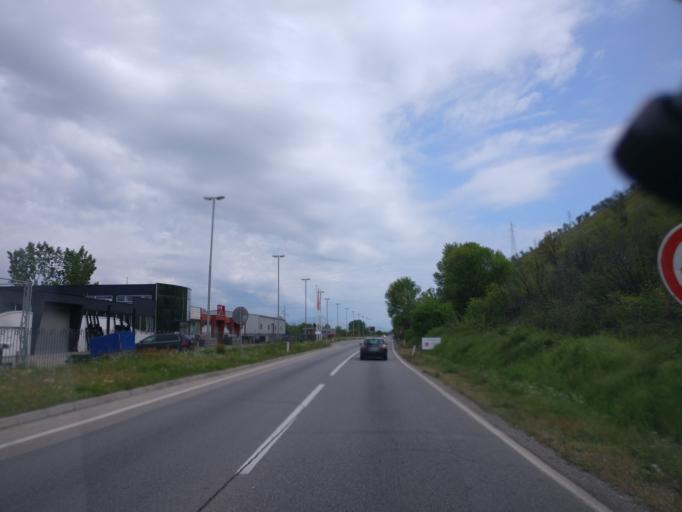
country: ME
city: Spuz
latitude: 42.4529
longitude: 19.1950
